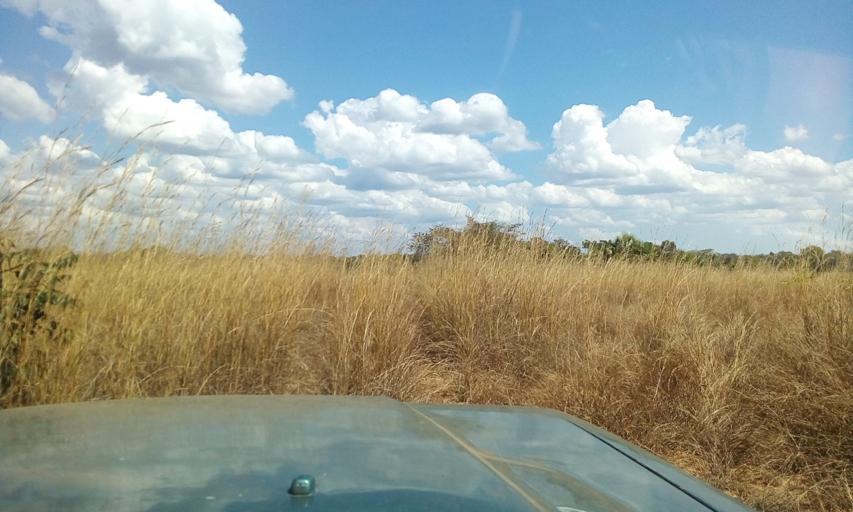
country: MG
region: Melaky
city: Mahabe
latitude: -16.4369
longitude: 45.3804
